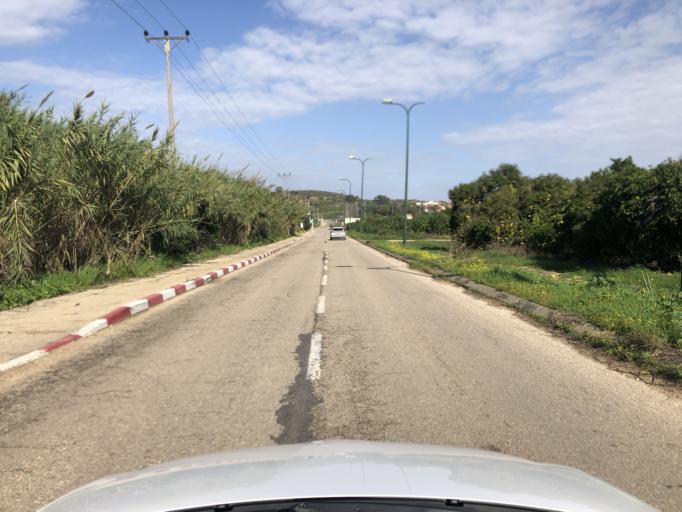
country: IL
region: Central District
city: Ness Ziona
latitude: 31.9169
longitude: 34.7787
